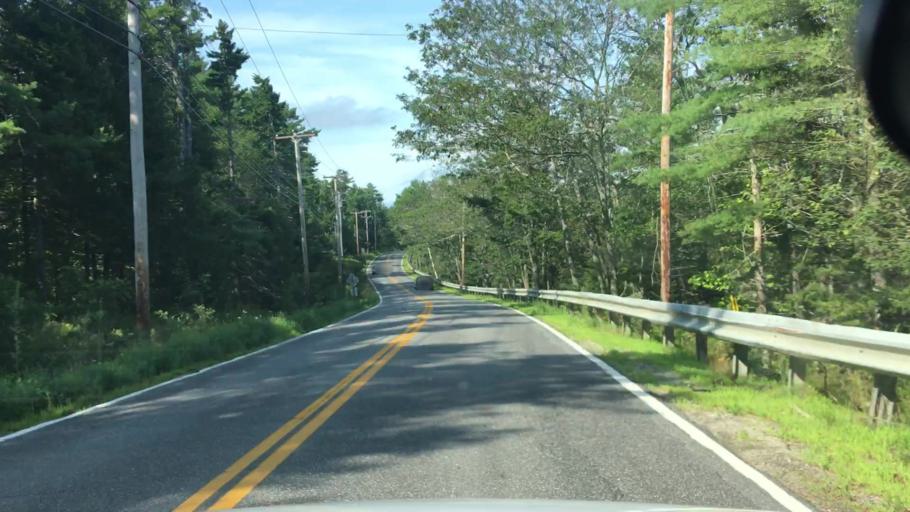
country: US
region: Maine
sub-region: Cumberland County
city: Harpswell Center
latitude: 43.7911
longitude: -69.9479
